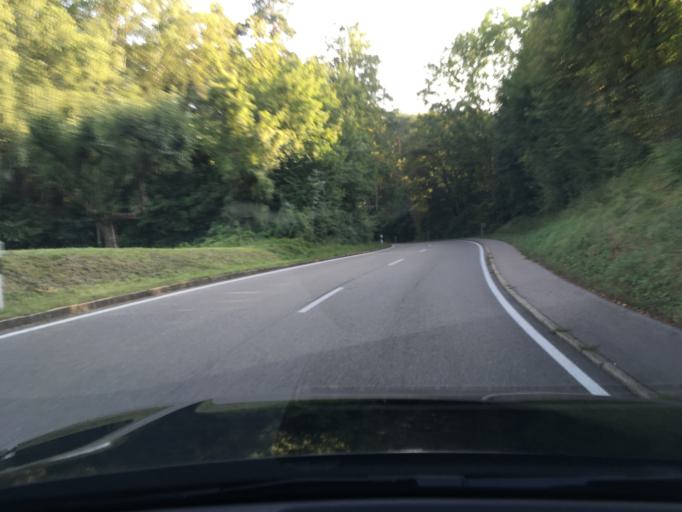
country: DE
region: Baden-Wuerttemberg
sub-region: Regierungsbezirk Stuttgart
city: Schorndorf
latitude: 48.7986
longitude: 9.5485
